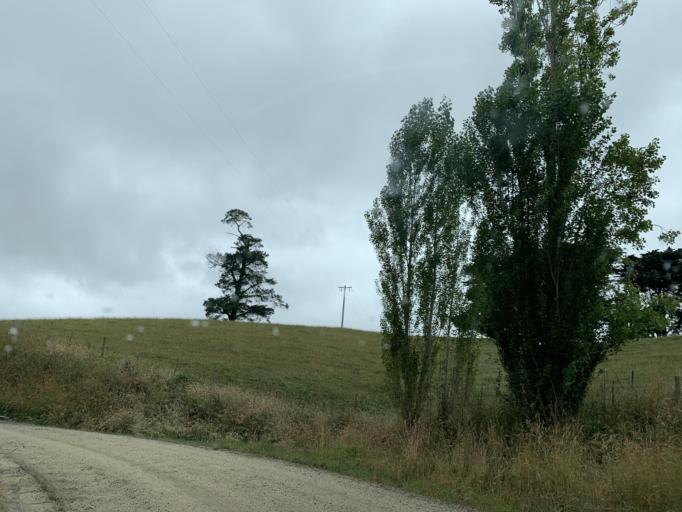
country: AU
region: Victoria
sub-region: Baw Baw
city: Warragul
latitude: -38.3045
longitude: 145.8970
